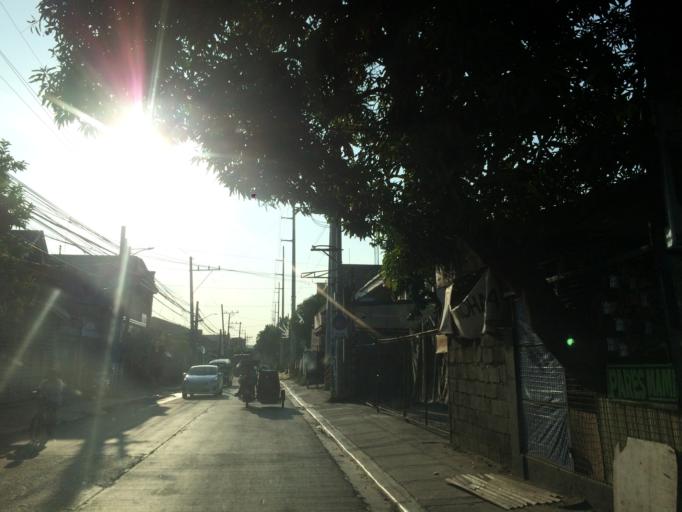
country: PH
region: Calabarzon
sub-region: Province of Rizal
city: San Mateo
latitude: 14.6808
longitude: 121.1202
